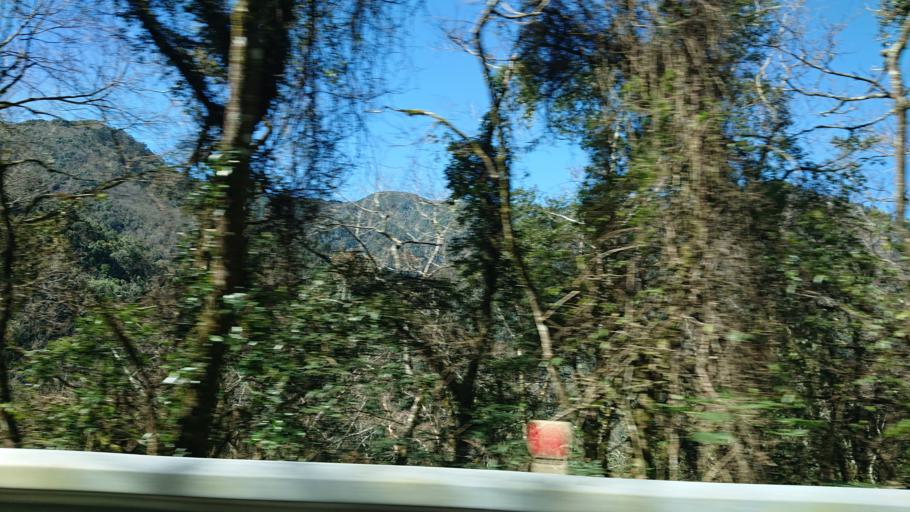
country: TW
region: Taiwan
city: Daxi
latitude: 24.4057
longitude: 121.3667
